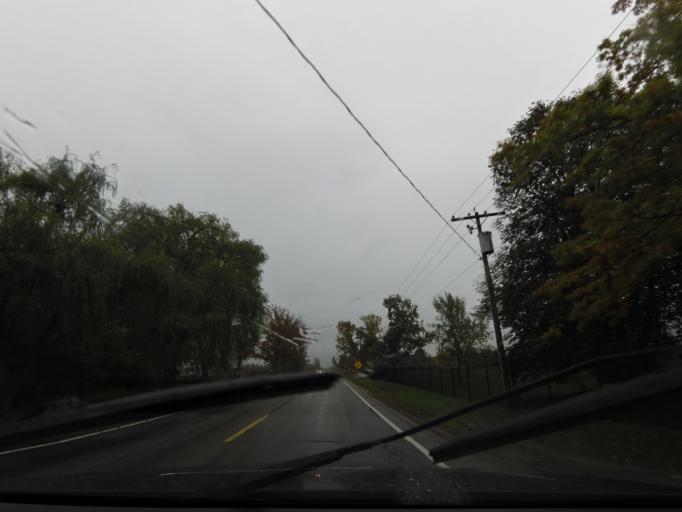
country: CA
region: Ontario
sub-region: Halton
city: Milton
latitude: 43.4497
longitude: -79.8807
